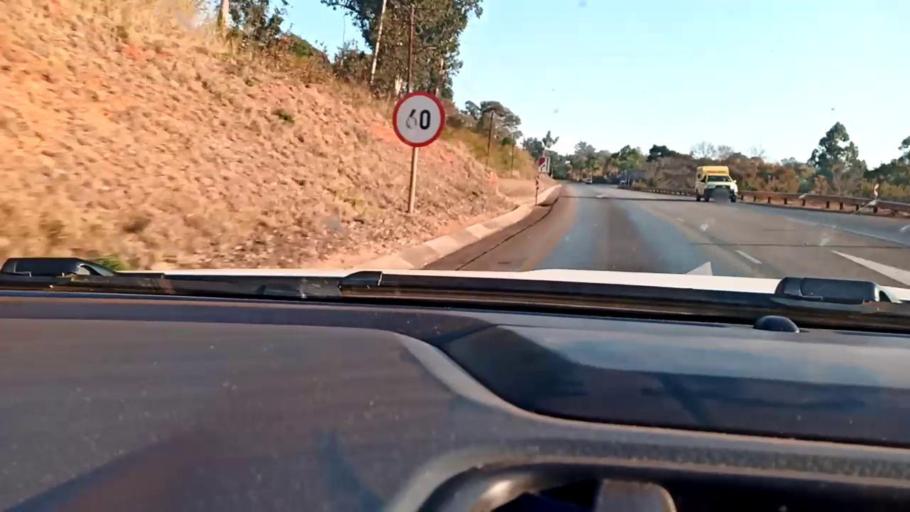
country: ZA
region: Limpopo
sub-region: Mopani District Municipality
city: Duiwelskloof
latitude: -23.6876
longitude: 30.1477
